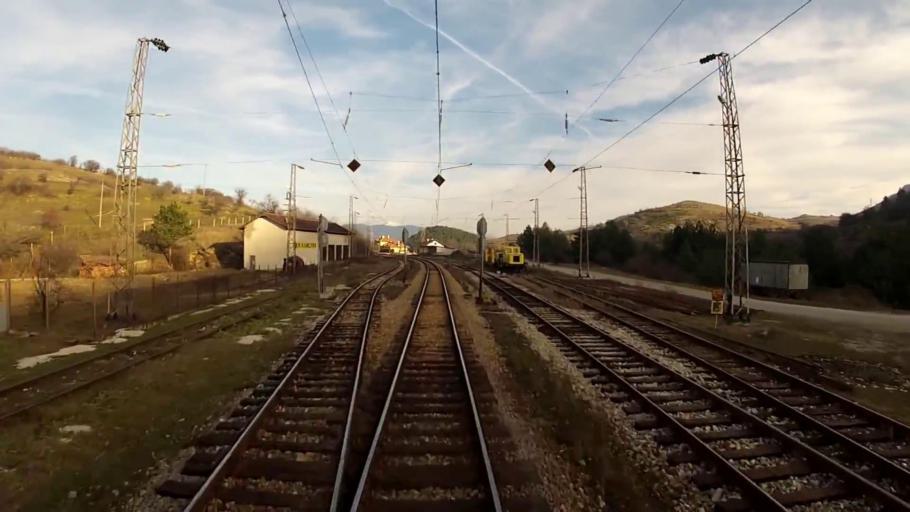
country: BG
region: Plovdiv
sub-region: Obshtina Karlovo
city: Klisura
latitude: 42.7051
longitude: 24.5036
